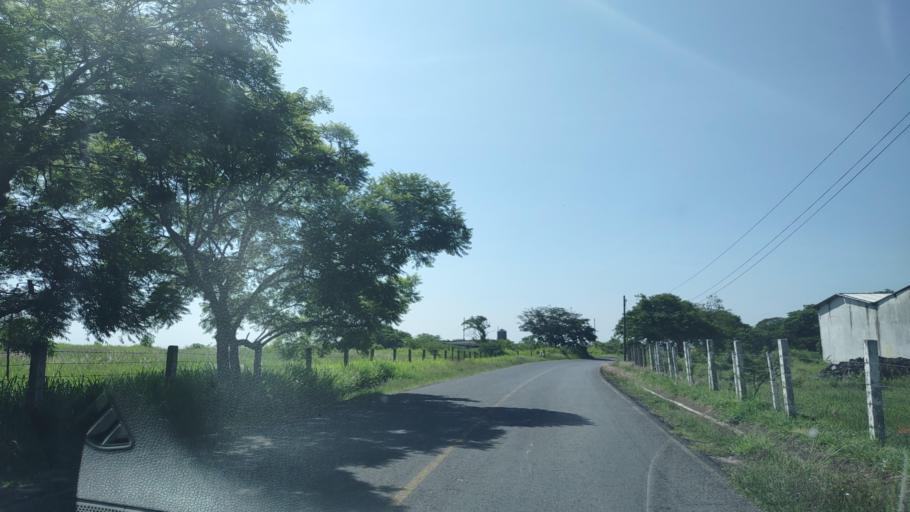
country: MX
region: Veracruz
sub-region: Emiliano Zapata
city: Dos Rios
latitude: 19.4942
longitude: -96.8243
